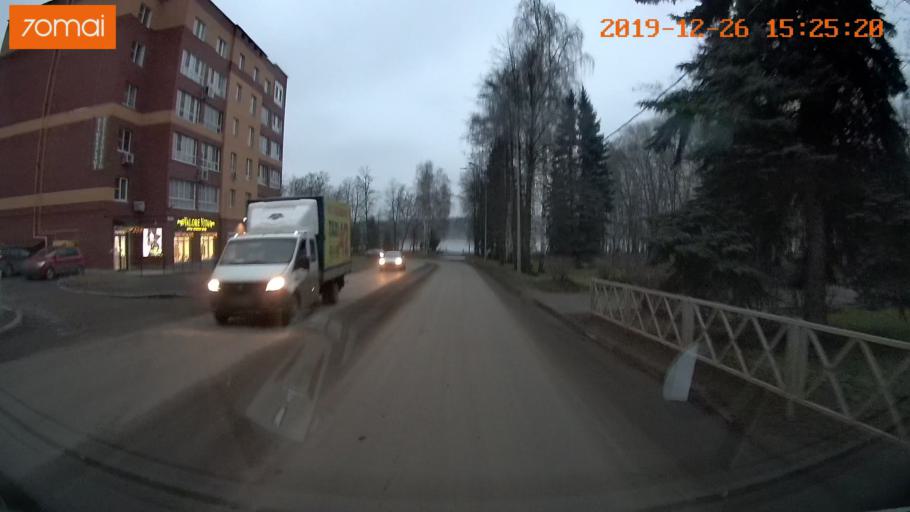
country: RU
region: Jaroslavl
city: Rybinsk
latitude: 58.0530
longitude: 38.8389
